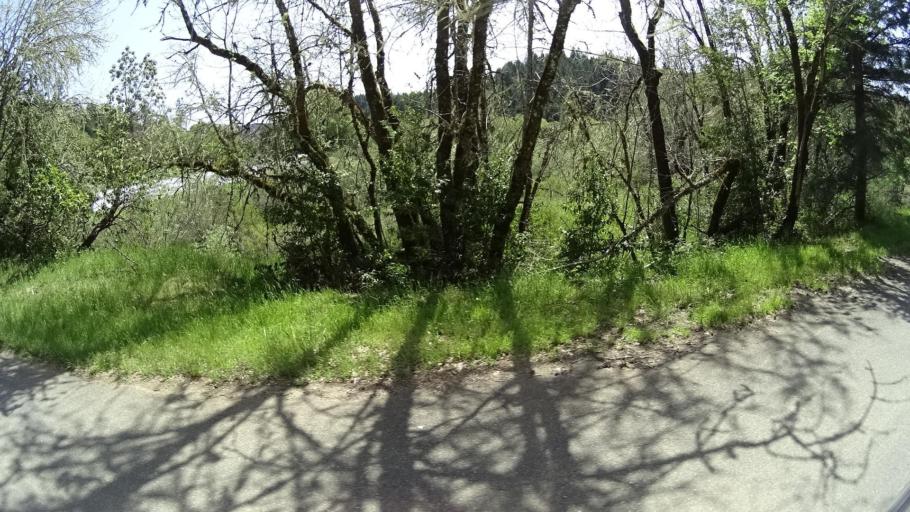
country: US
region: California
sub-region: Humboldt County
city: Redway
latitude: 40.3097
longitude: -123.6558
